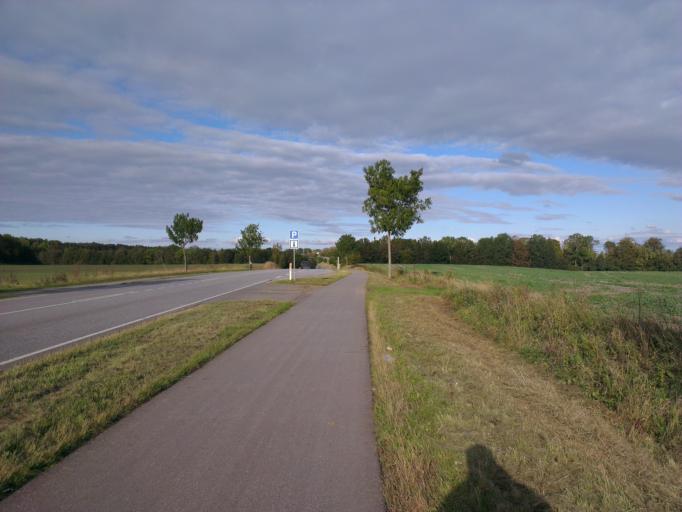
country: DK
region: Capital Region
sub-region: Frederikssund Kommune
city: Skibby
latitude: 55.7345
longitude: 11.9479
